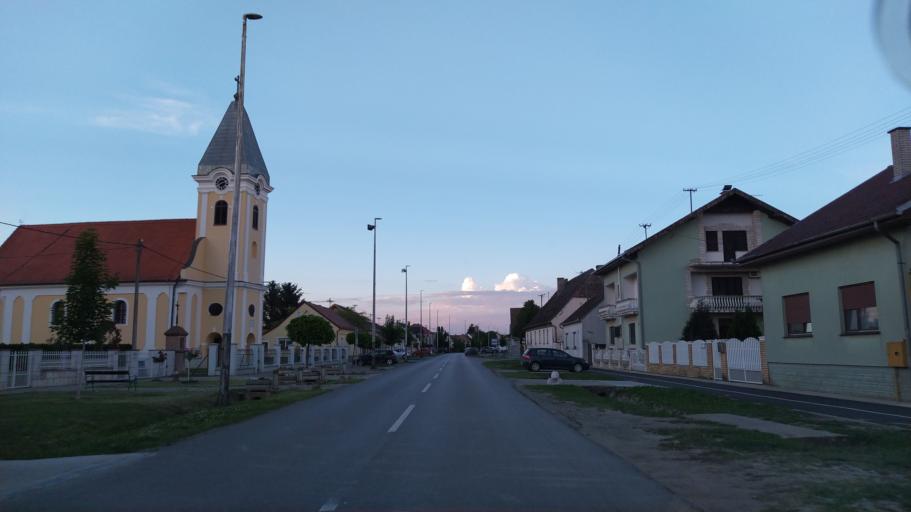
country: HR
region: Osjecko-Baranjska
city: Cepin
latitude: 45.5195
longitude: 18.5535
